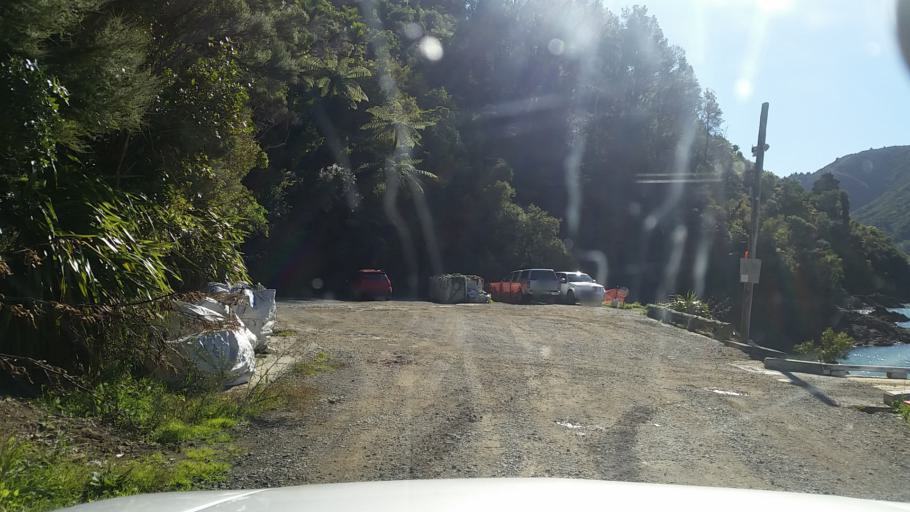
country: NZ
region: Marlborough
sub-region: Marlborough District
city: Picton
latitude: -41.1031
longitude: 173.6582
